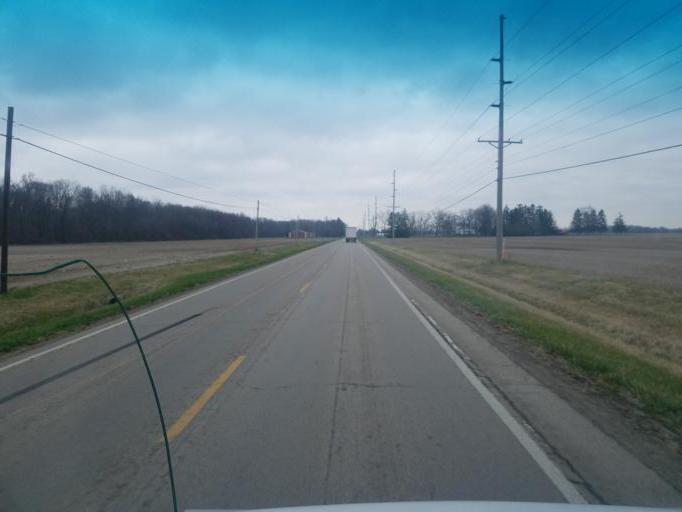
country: US
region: Ohio
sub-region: Defiance County
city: Hicksville
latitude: 41.2694
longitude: -84.7621
